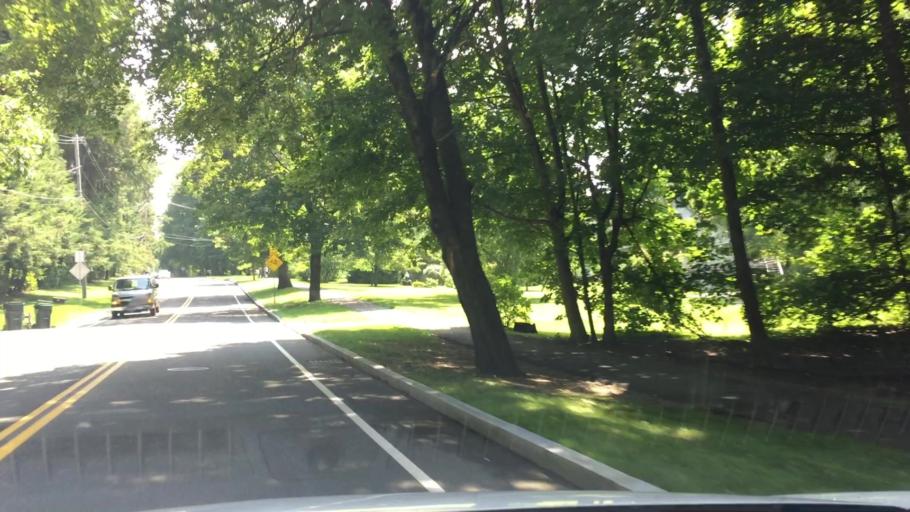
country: US
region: Massachusetts
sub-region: Berkshire County
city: Lenox
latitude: 42.3570
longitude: -73.2897
